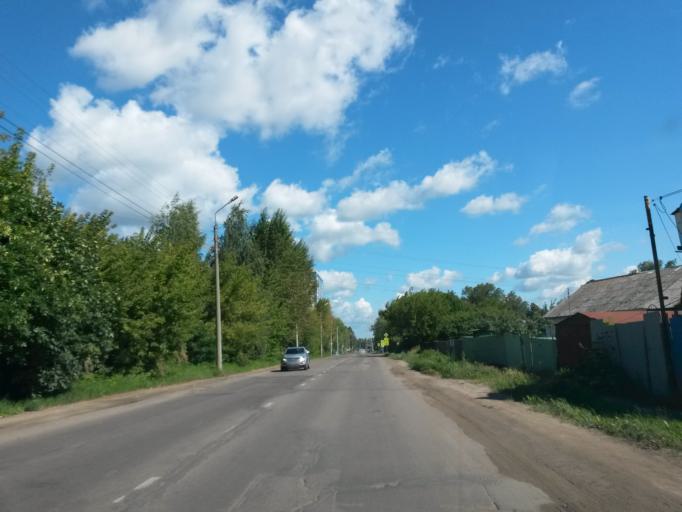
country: RU
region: Jaroslavl
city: Yaroslavl
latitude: 57.5821
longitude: 39.8720
